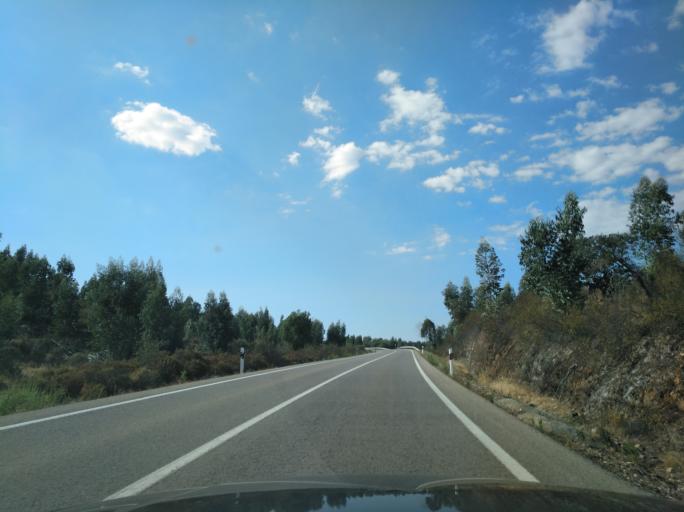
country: ES
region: Andalusia
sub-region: Provincia de Huelva
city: Santa Barbara de Casa
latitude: 37.8050
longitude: -7.2023
